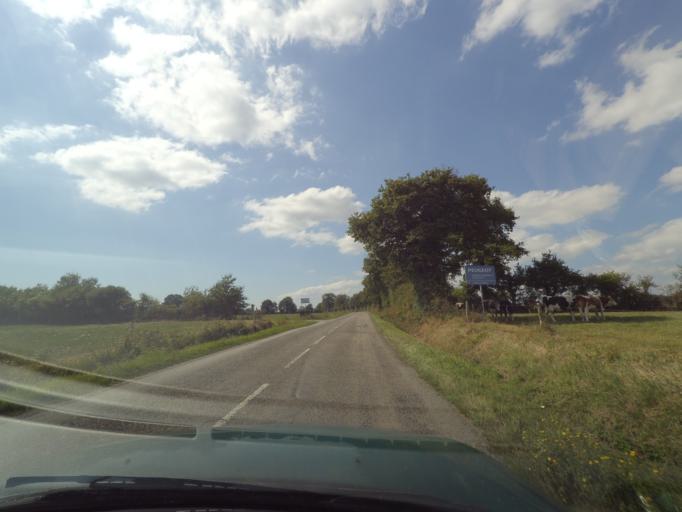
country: FR
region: Pays de la Loire
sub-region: Departement de la Loire-Atlantique
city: Saint-Hilaire-de-Chaleons
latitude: 47.0986
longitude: -1.8402
